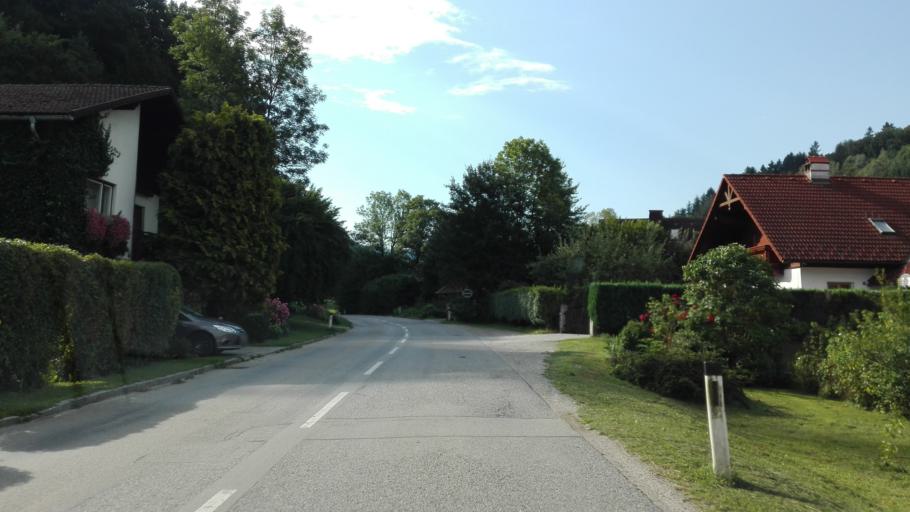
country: AT
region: Lower Austria
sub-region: Politischer Bezirk Sankt Polten
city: Kasten bei Boheimkirchen
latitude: 48.1149
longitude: 15.7552
